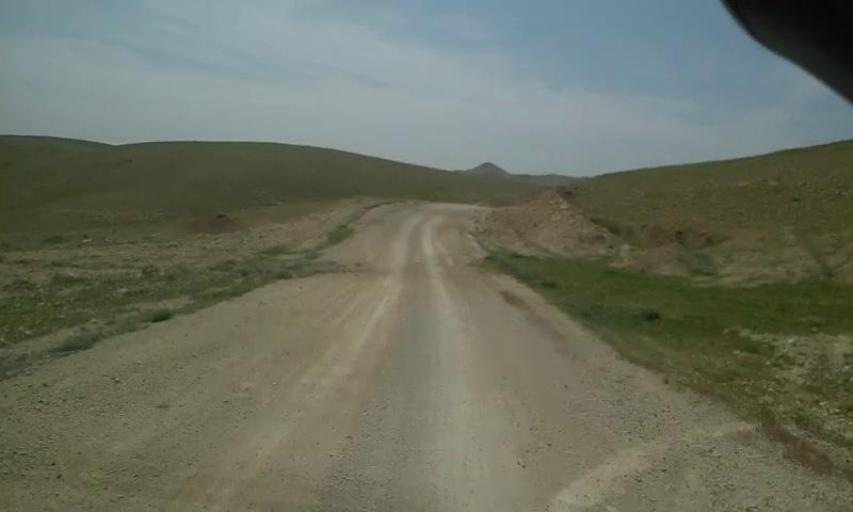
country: PS
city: `Arab ar Rashaydah
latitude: 31.4937
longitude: 35.2915
